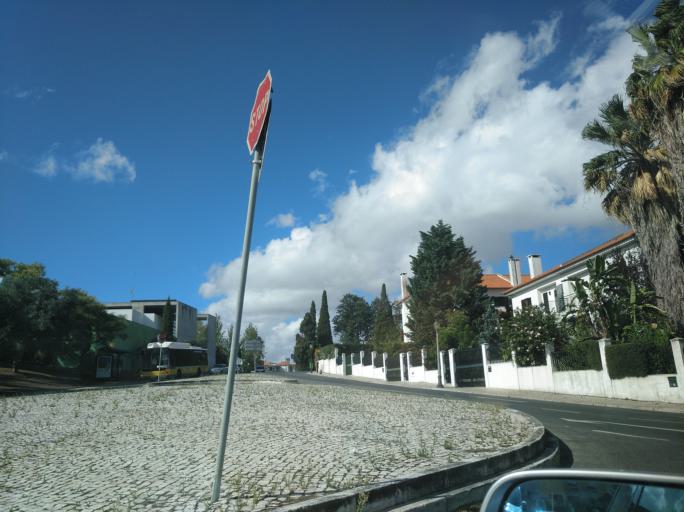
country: PT
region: Lisbon
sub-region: Loures
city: Moscavide
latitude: 38.7721
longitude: -9.1174
